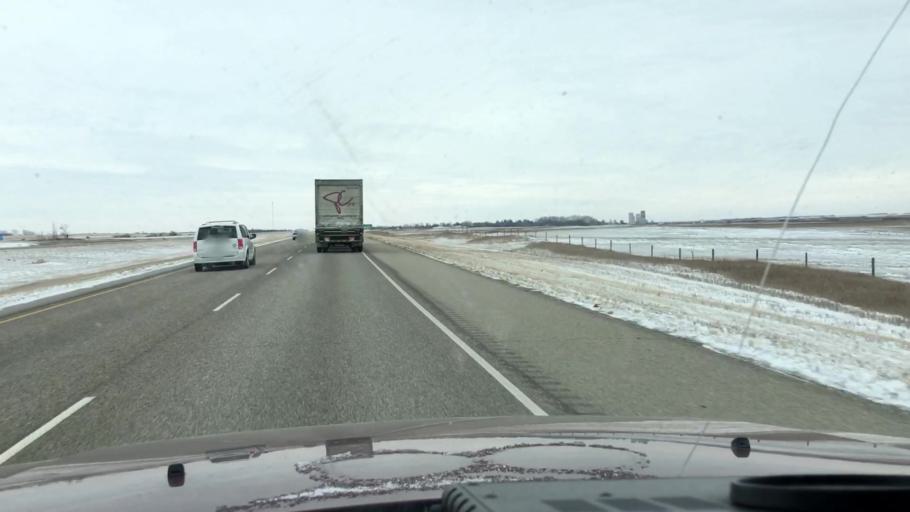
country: CA
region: Saskatchewan
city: Saskatoon
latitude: 51.5197
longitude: -106.2929
